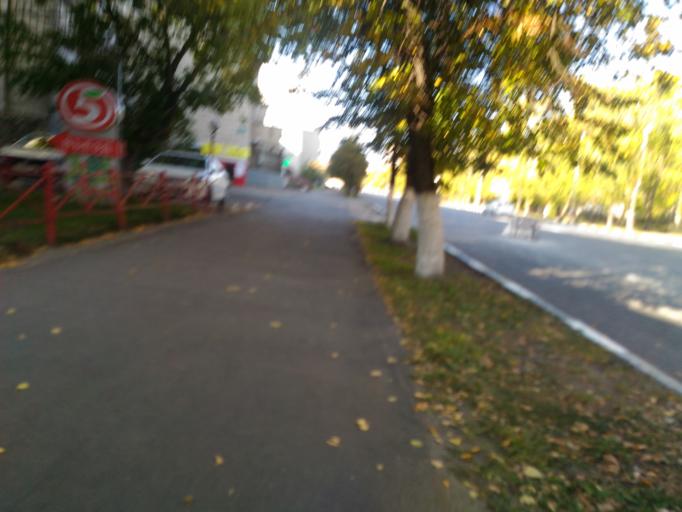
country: RU
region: Ulyanovsk
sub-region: Ulyanovskiy Rayon
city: Ulyanovsk
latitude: 54.3021
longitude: 48.3788
